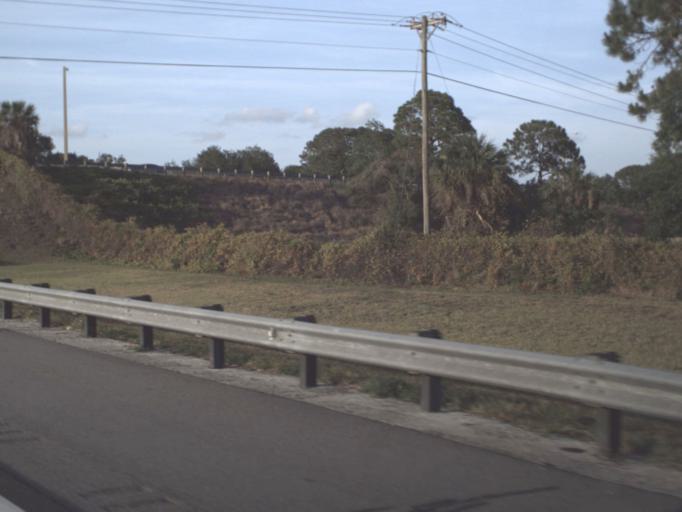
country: US
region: Florida
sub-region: Brevard County
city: Port Saint John
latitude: 28.4640
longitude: -80.8211
